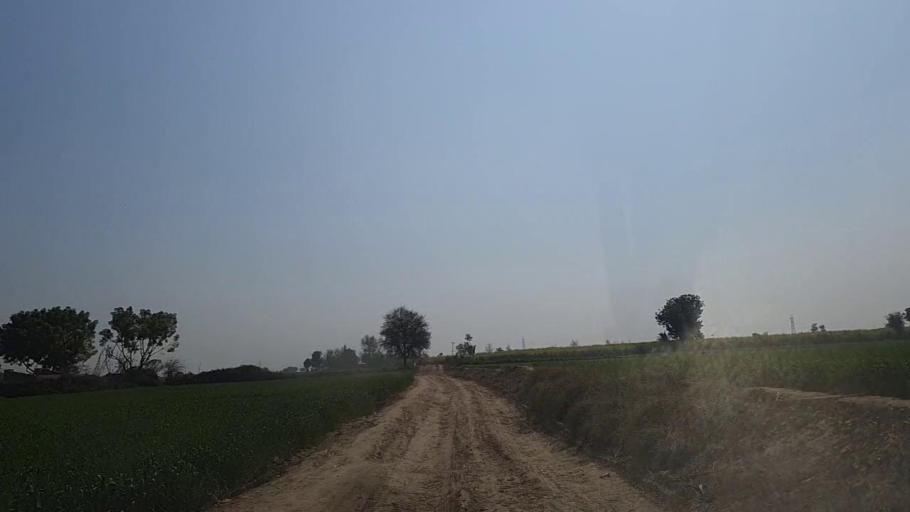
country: PK
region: Sindh
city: Moro
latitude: 26.6971
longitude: 67.9278
